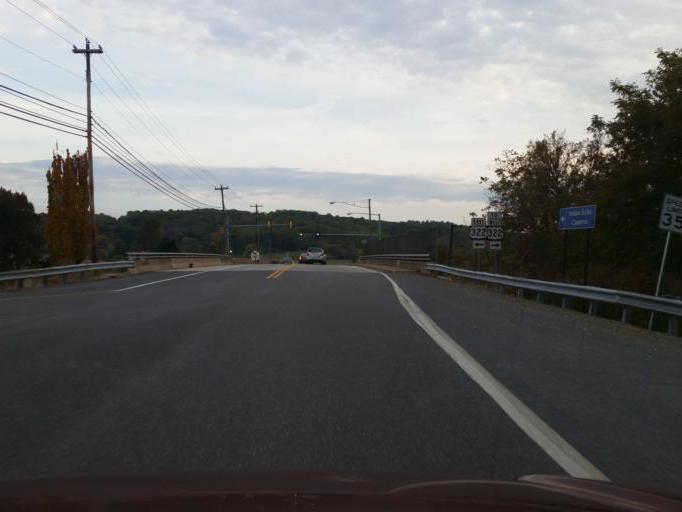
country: US
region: Pennsylvania
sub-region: Dauphin County
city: Hummelstown
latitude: 40.2593
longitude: -76.7001
